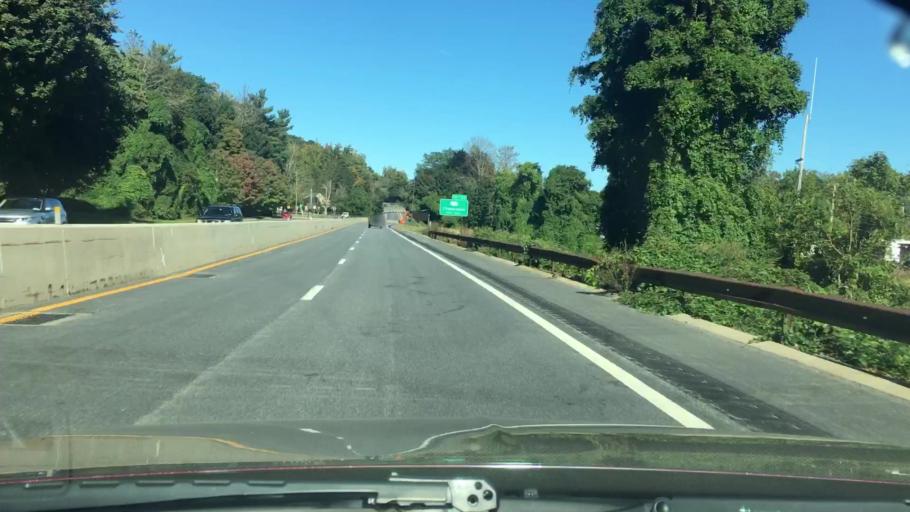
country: US
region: New York
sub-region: Westchester County
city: Chappaqua
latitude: 41.1560
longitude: -73.7773
